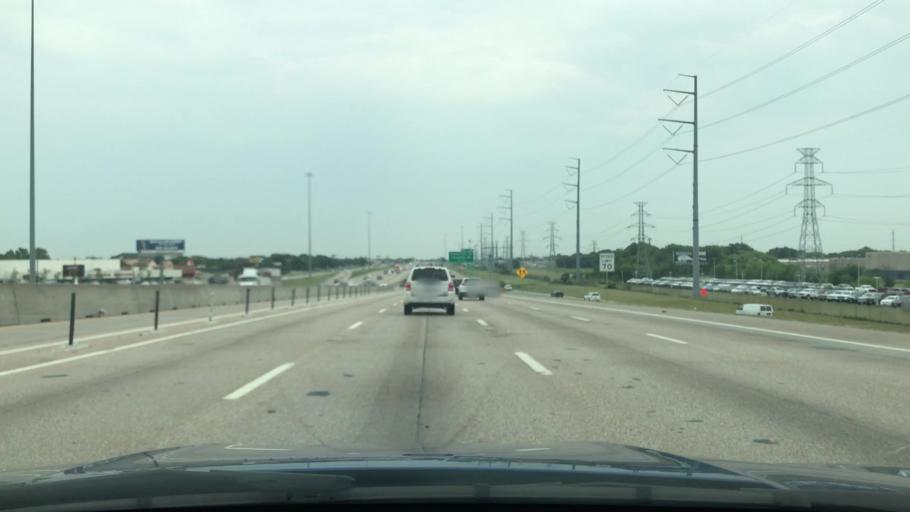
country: US
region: Texas
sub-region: Dallas County
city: Garland
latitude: 32.8644
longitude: -96.6608
